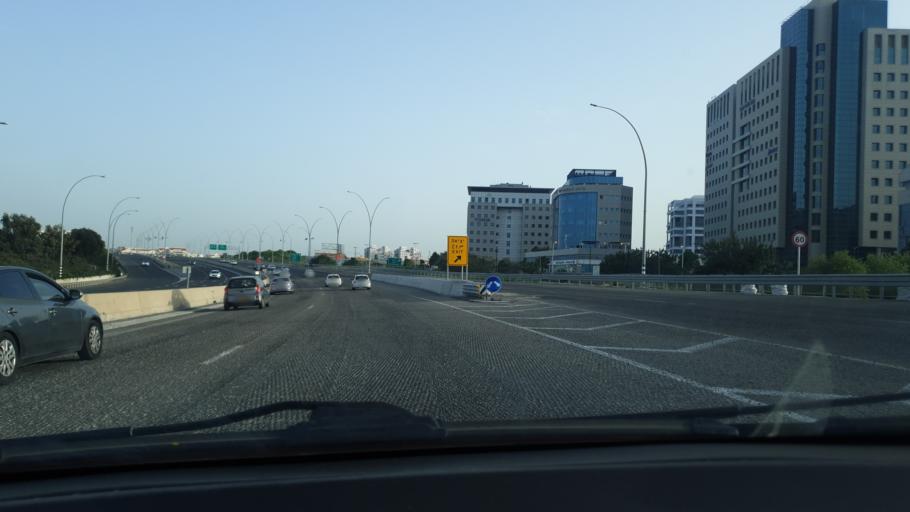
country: IL
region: Central District
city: Ra'anana
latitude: 32.1981
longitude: 34.8848
